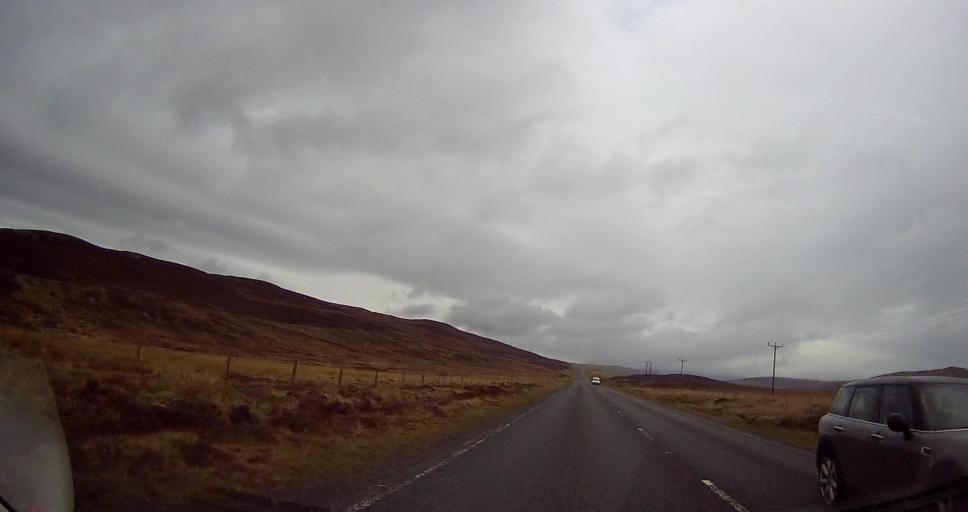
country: GB
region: Scotland
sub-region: Shetland Islands
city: Lerwick
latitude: 60.2082
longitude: -1.2334
